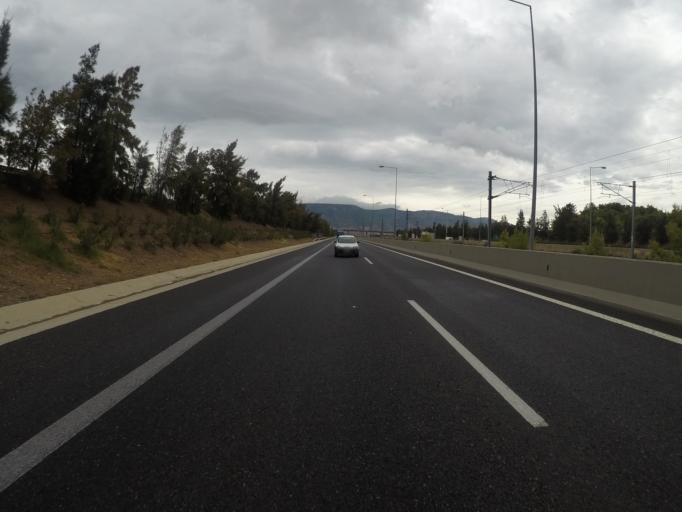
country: GR
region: Attica
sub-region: Nomarchia Dytikis Attikis
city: Magoula
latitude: 38.0811
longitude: 23.5366
